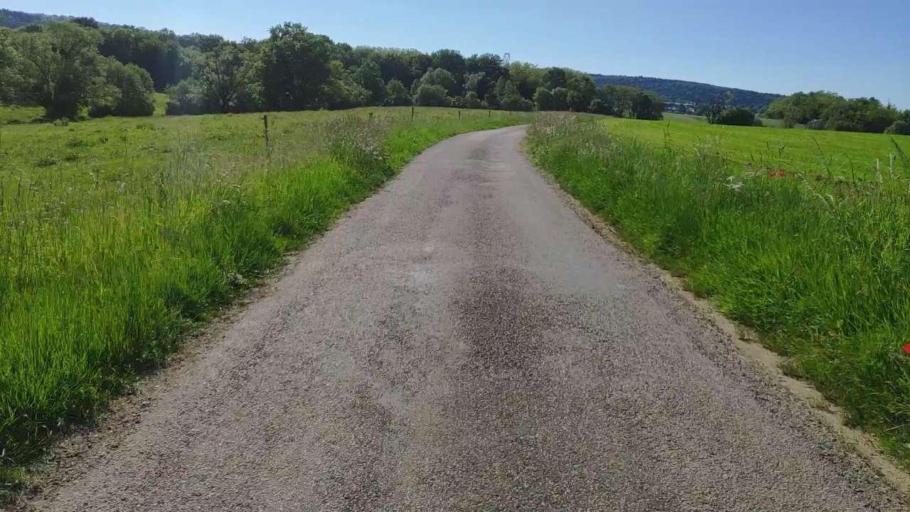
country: FR
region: Franche-Comte
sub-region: Departement du Jura
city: Perrigny
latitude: 46.7244
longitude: 5.5721
